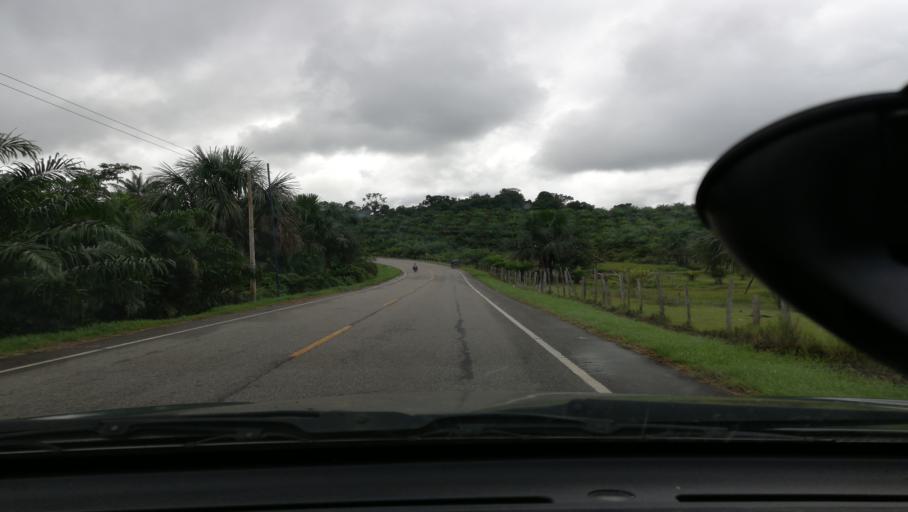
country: PE
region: Loreto
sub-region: Provincia de Loreto
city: Nauta
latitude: -4.4837
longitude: -73.5965
